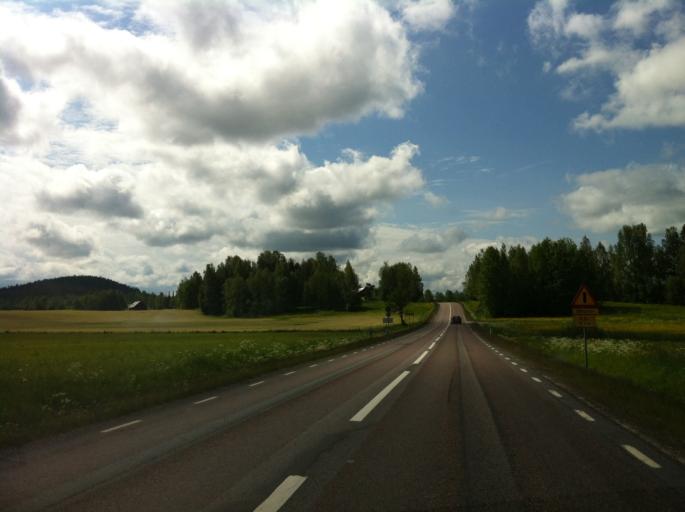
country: SE
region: Vaermland
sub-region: Sunne Kommun
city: Sunne
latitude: 59.6463
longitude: 13.1559
